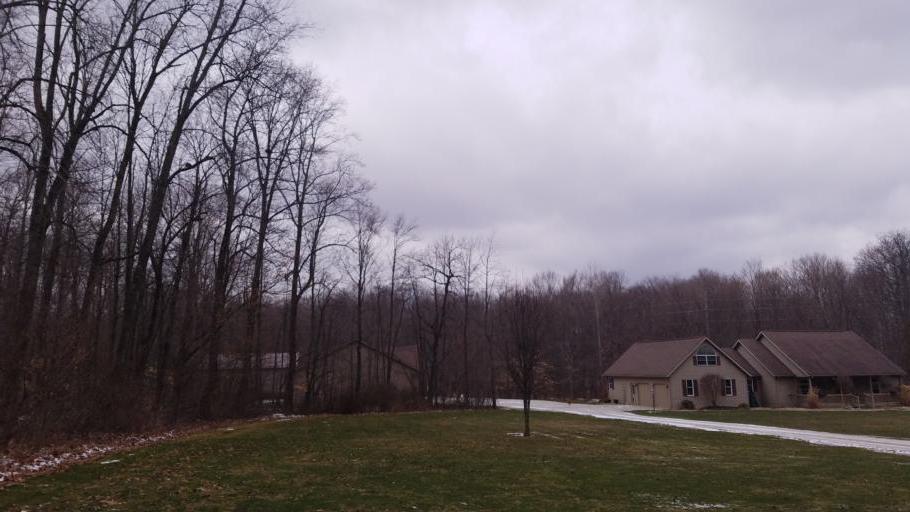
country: US
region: Ohio
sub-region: Crawford County
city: Galion
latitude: 40.6602
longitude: -82.7089
